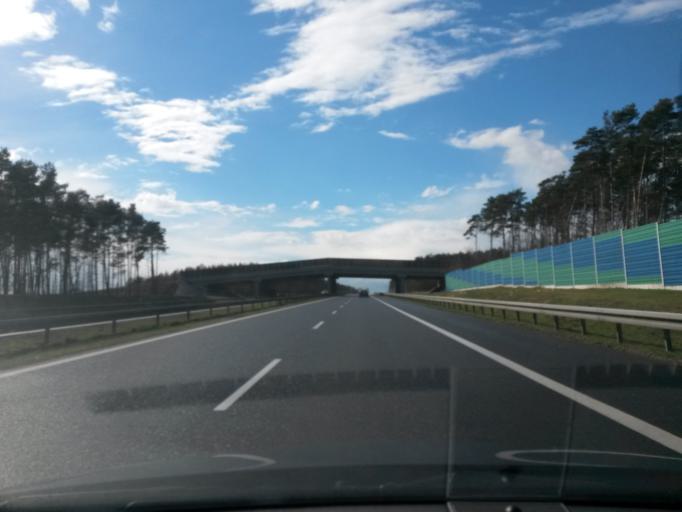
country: PL
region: Greater Poland Voivodeship
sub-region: Powiat slupecki
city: Strzalkowo
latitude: 52.2638
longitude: 17.7584
